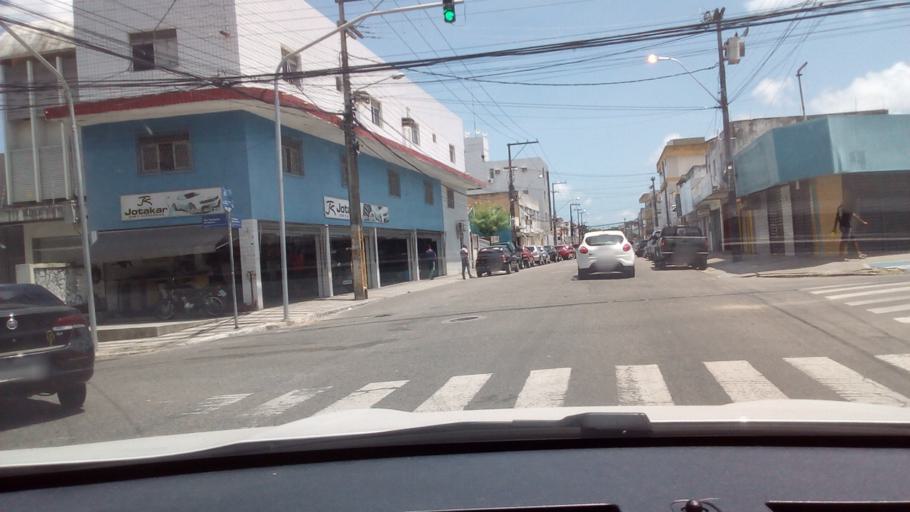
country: BR
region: Paraiba
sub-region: Joao Pessoa
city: Joao Pessoa
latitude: -7.1229
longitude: -34.8838
